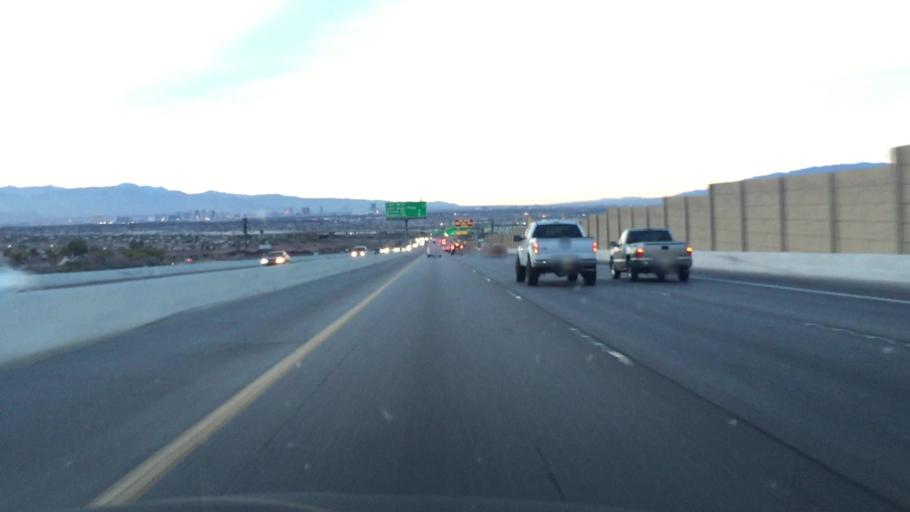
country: US
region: Nevada
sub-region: Clark County
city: Henderson
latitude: 36.0218
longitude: -115.0007
